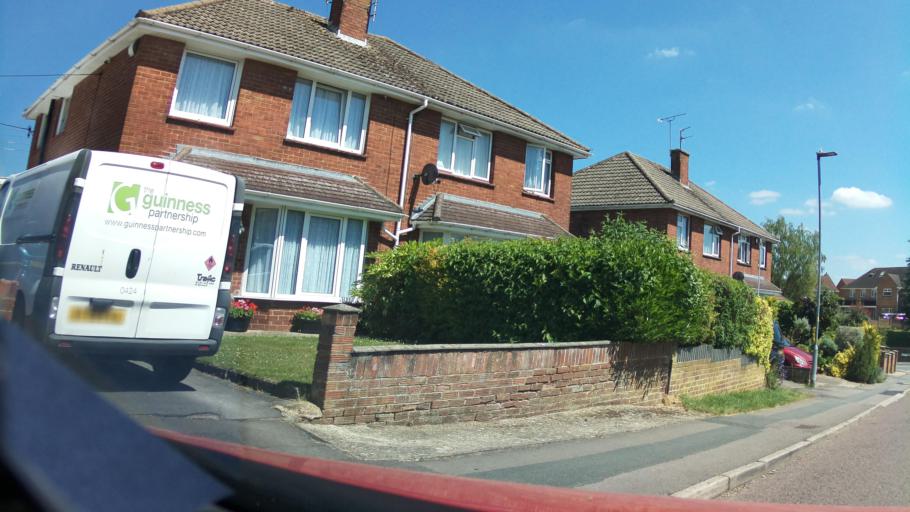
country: GB
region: England
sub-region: Wiltshire
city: Royal Wootton Bassett
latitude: 51.5441
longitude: -1.8916
